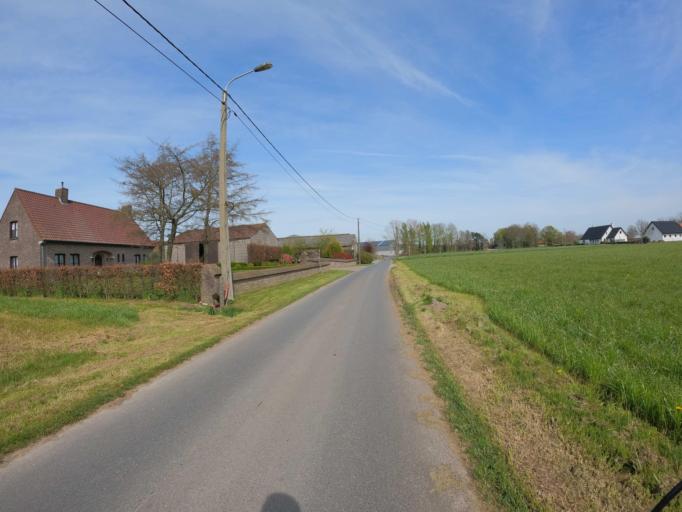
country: BE
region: Flanders
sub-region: Provincie West-Vlaanderen
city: Ruiselede
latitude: 51.0278
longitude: 3.3664
